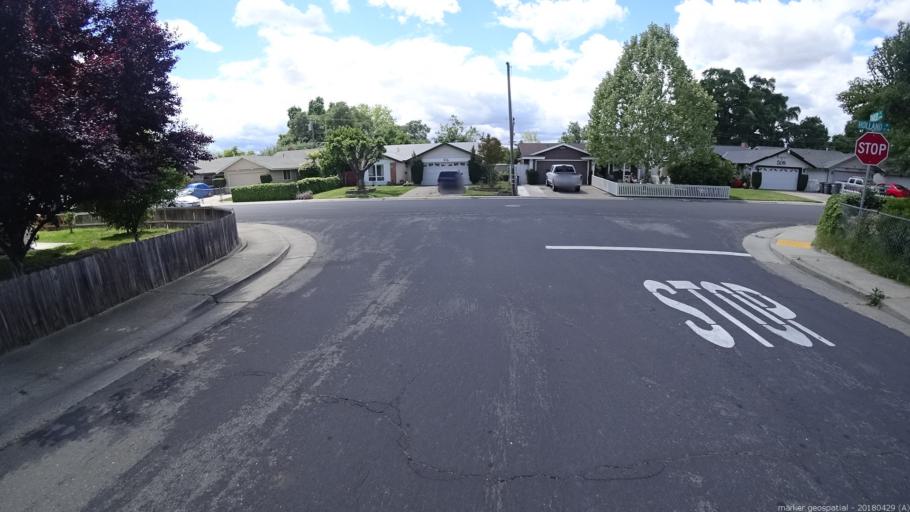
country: US
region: California
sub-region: Yolo County
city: West Sacramento
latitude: 38.5975
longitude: -121.5303
